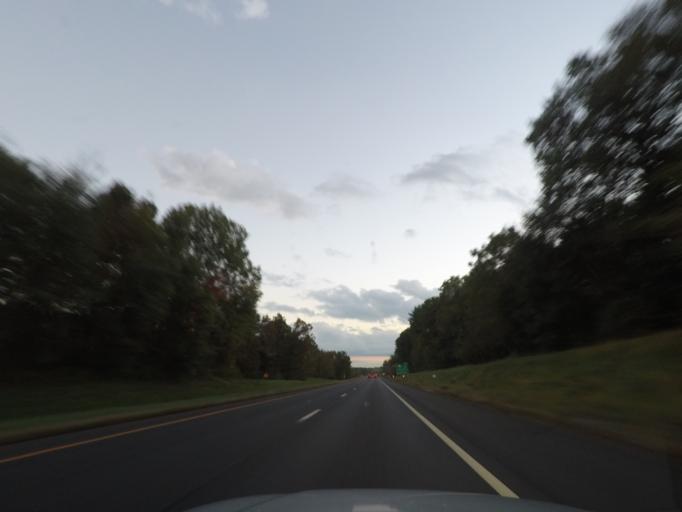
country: US
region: New York
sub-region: Ulster County
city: New Paltz
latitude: 41.7544
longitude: -74.0596
